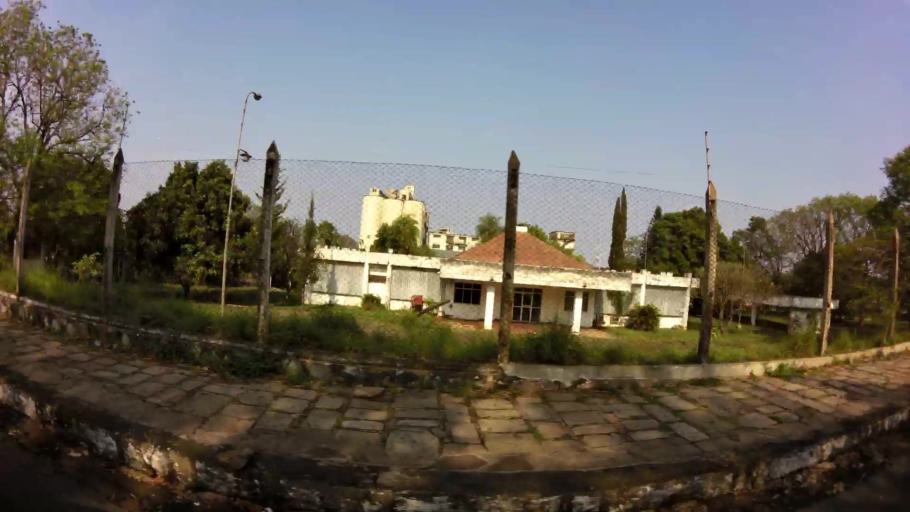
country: PY
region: Presidente Hayes
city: Nanawa
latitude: -25.2842
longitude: -57.6643
